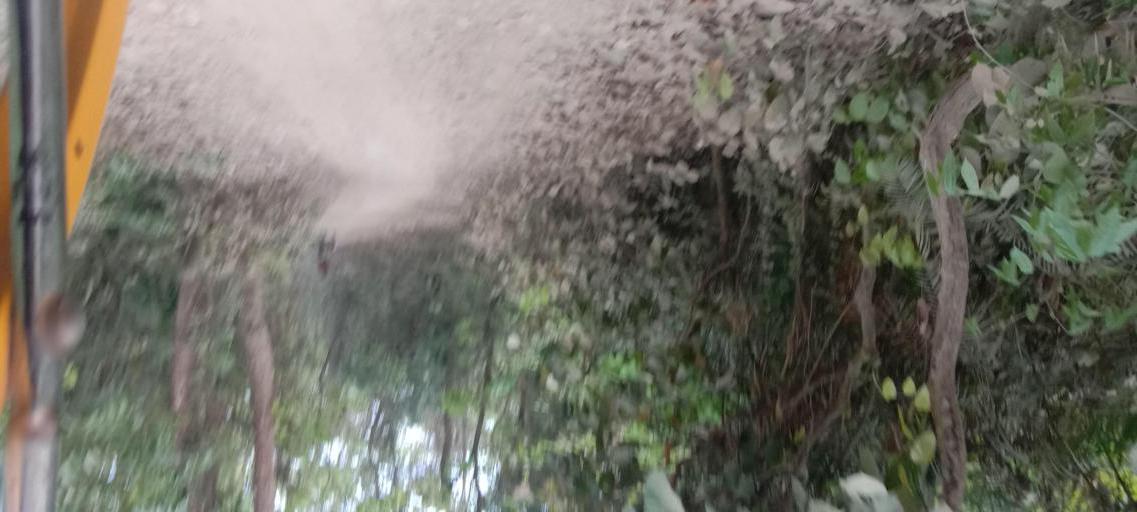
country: BD
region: Dhaka
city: Sakhipur
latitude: 24.3288
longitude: 90.3269
